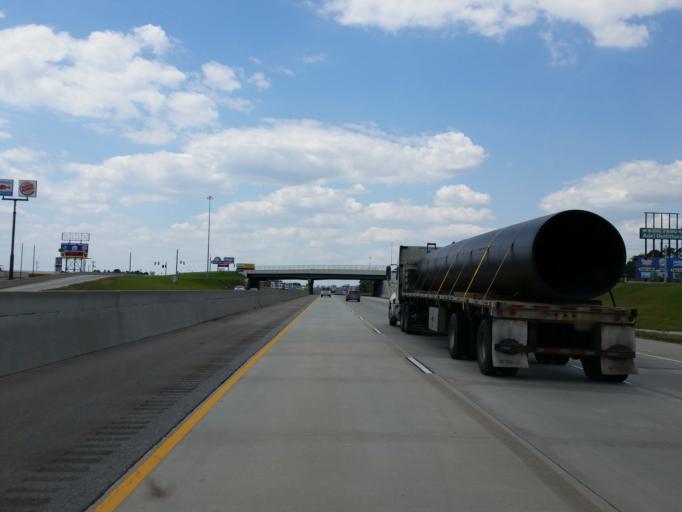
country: US
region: Georgia
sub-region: Cook County
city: Adel
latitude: 31.1337
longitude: -83.4380
